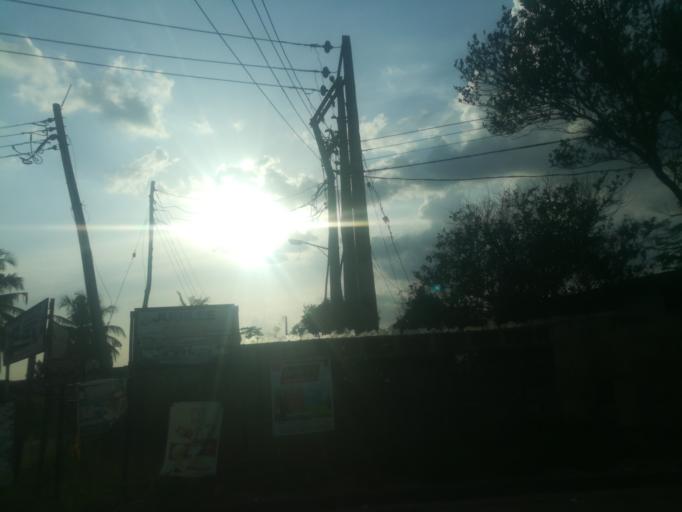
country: NG
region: Ogun
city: Abeokuta
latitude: 7.1272
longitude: 3.3206
